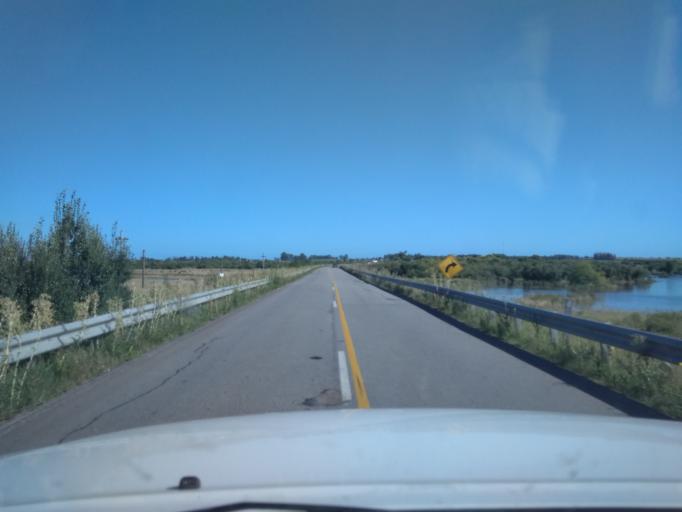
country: UY
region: Canelones
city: San Ramon
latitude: -34.3298
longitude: -55.9606
